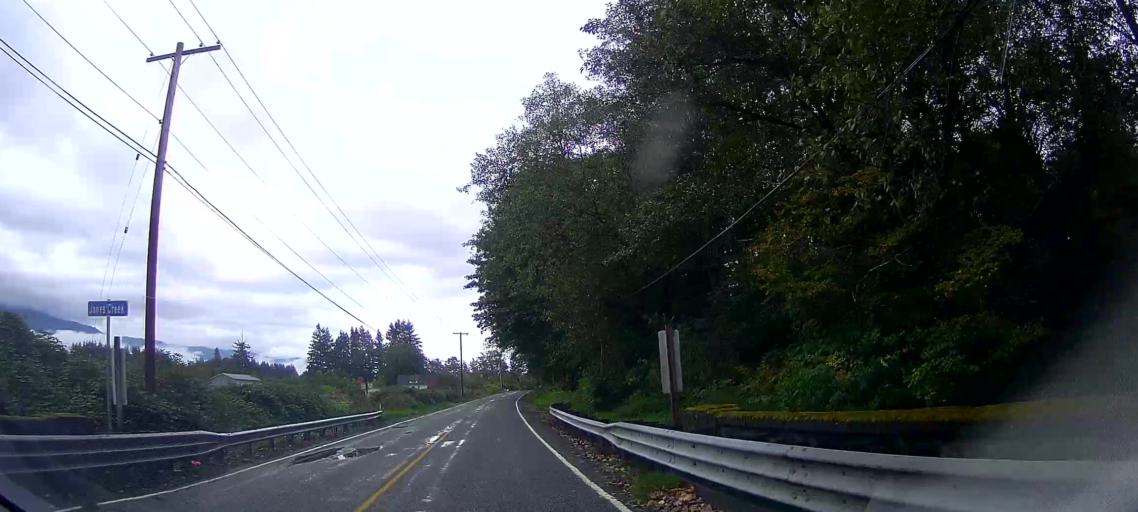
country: US
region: Washington
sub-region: Skagit County
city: Sedro-Woolley
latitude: 48.5275
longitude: -122.0513
